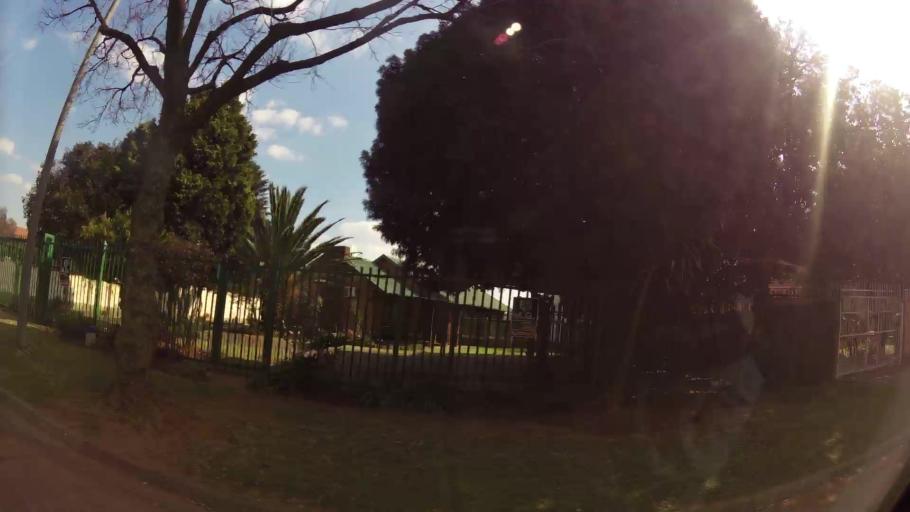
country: ZA
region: Gauteng
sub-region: Ekurhuleni Metropolitan Municipality
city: Germiston
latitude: -26.1914
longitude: 28.2003
